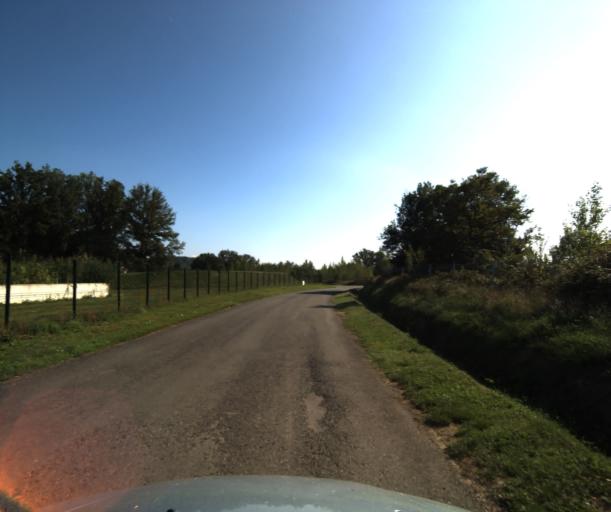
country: FR
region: Midi-Pyrenees
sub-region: Departement de la Haute-Garonne
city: Le Fauga
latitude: 43.4099
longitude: 1.3050
